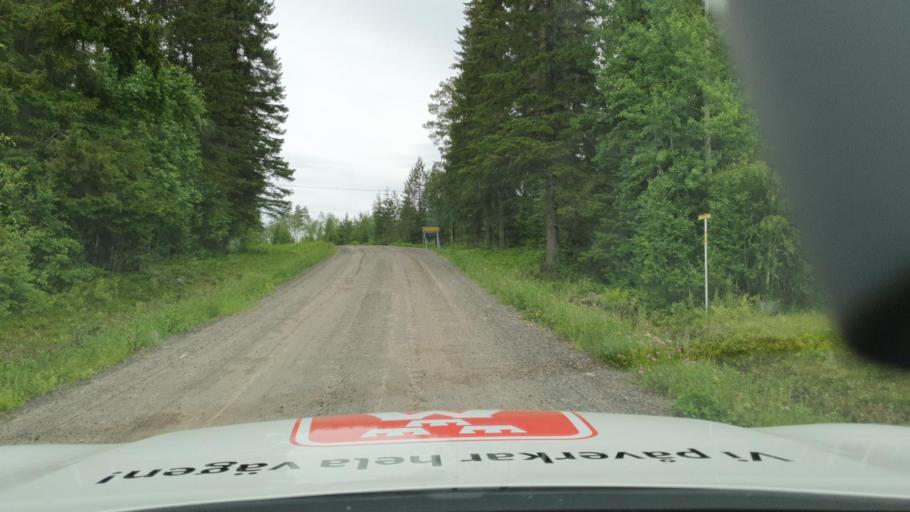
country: SE
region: Vaesterbotten
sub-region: Skelleftea Kommun
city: Burtraesk
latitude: 64.3630
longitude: 20.6168
